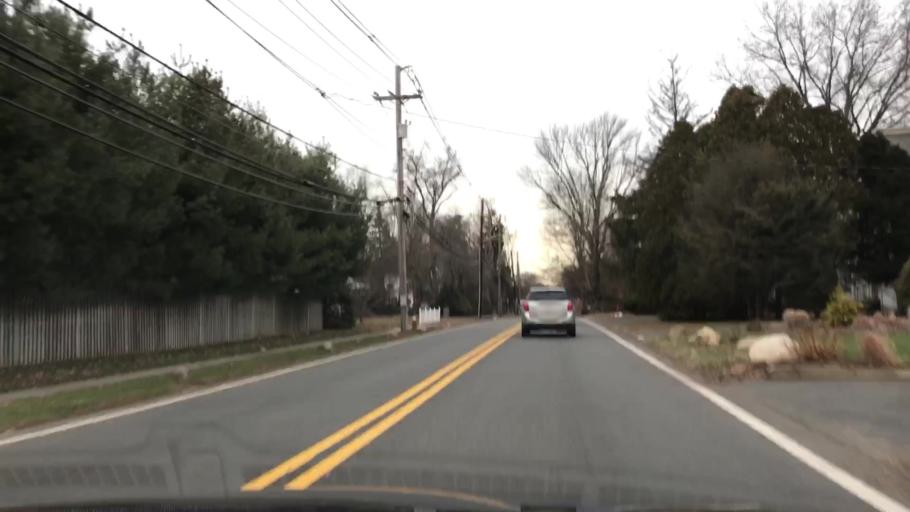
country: US
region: New Jersey
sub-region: Bergen County
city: Norwood
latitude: 40.9935
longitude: -73.9569
